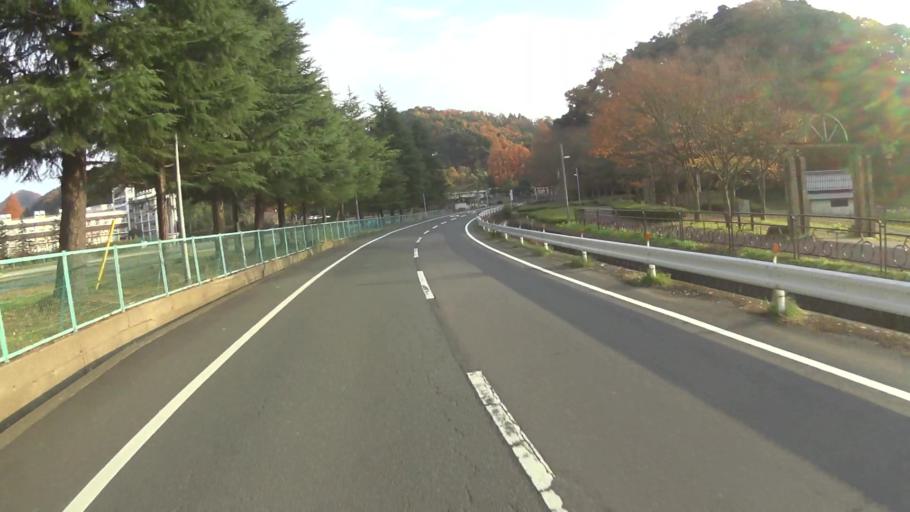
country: JP
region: Kyoto
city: Maizuru
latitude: 35.4970
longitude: 135.4374
